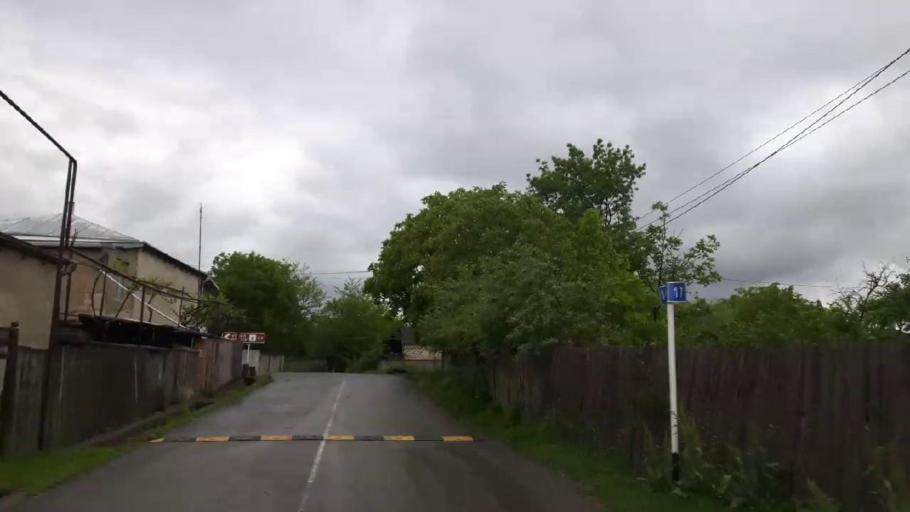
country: GE
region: Shida Kartli
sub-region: Khashuris Raioni
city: Khashuri
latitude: 41.9832
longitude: 43.6740
